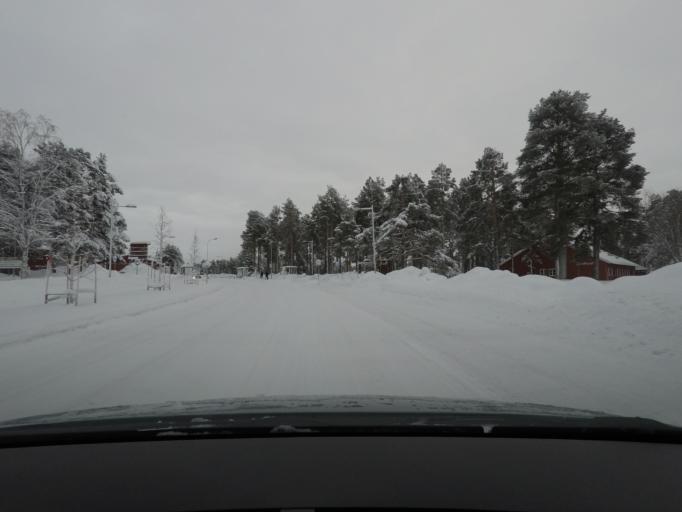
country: SE
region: Norrbotten
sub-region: Lulea Kommun
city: Lulea
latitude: 65.5927
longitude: 22.1886
